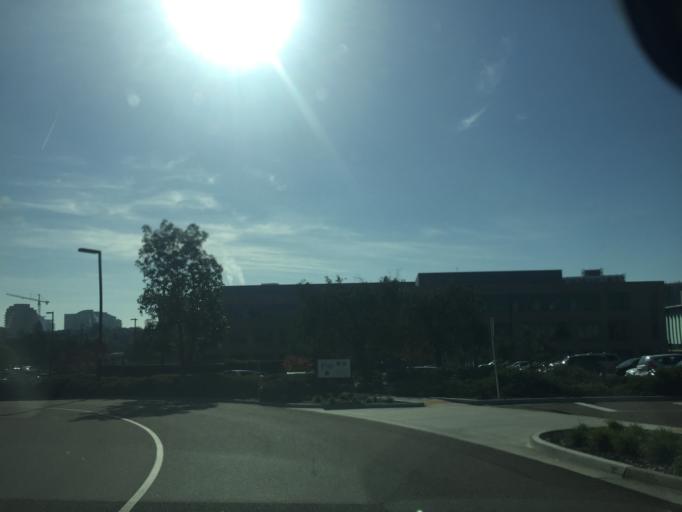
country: US
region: California
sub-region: San Diego County
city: La Jolla
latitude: 32.8784
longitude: -117.2199
